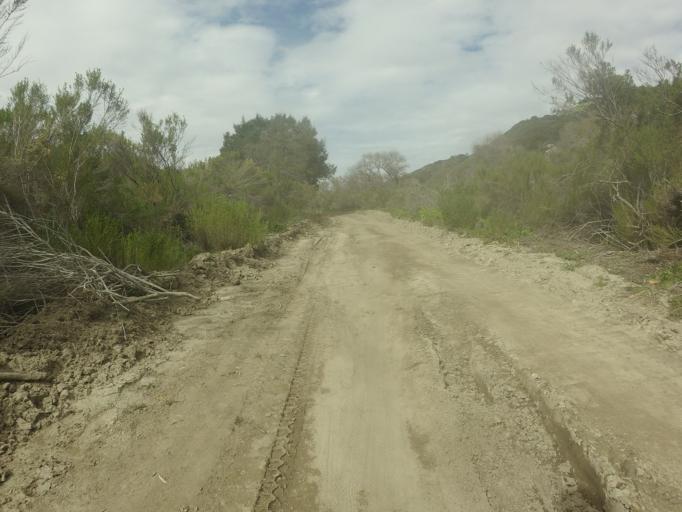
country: US
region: California
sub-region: Orange County
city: Aliso Viejo
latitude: 33.5452
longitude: -117.7395
